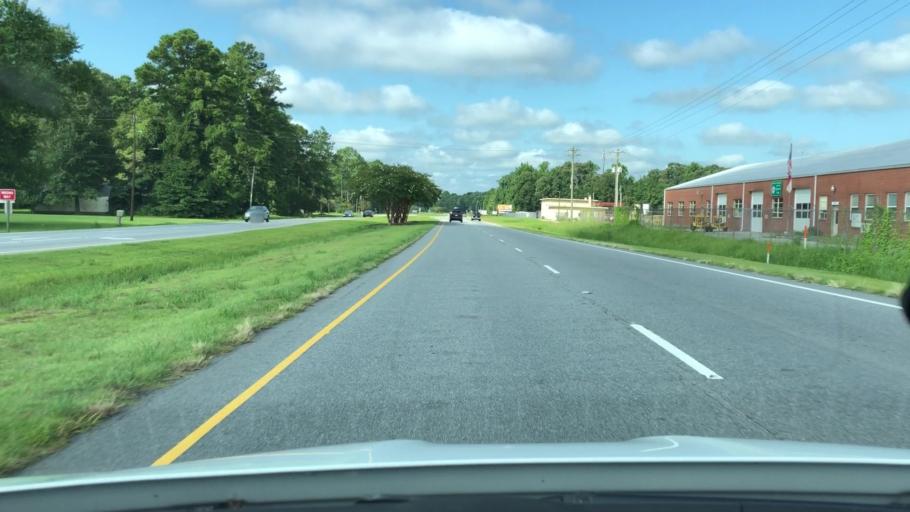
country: US
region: North Carolina
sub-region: Perquimans County
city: Hertford
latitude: 36.2121
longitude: -76.4362
